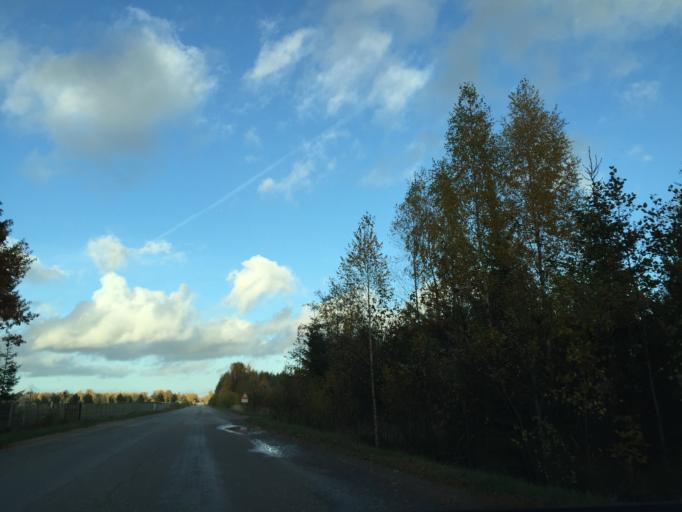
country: LV
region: Ogre
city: Jumprava
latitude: 56.7844
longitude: 25.0217
